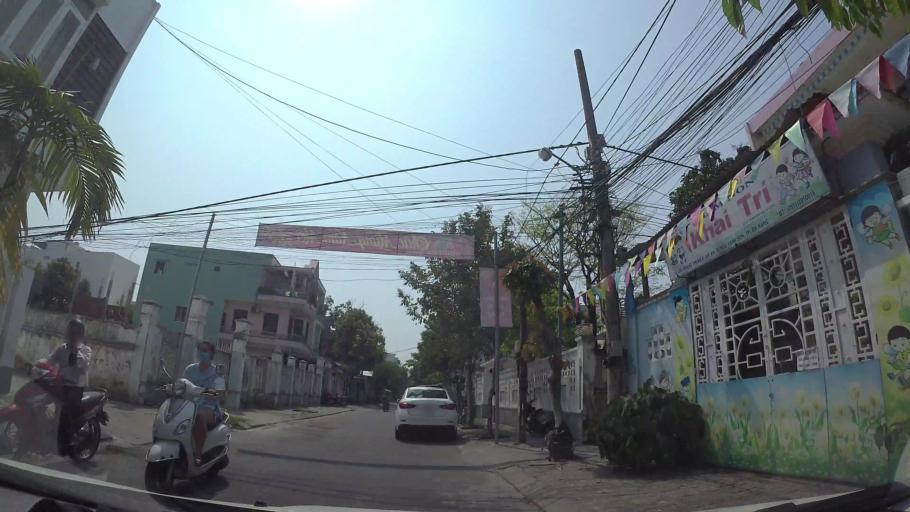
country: VN
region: Da Nang
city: Son Tra
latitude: 16.0409
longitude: 108.2452
